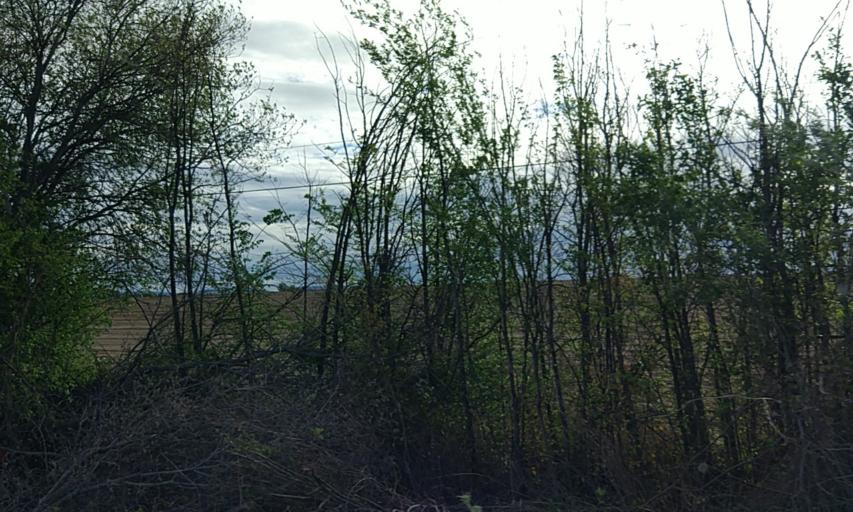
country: ES
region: Extremadura
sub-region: Provincia de Caceres
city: Moraleja
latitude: 40.0916
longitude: -6.6739
